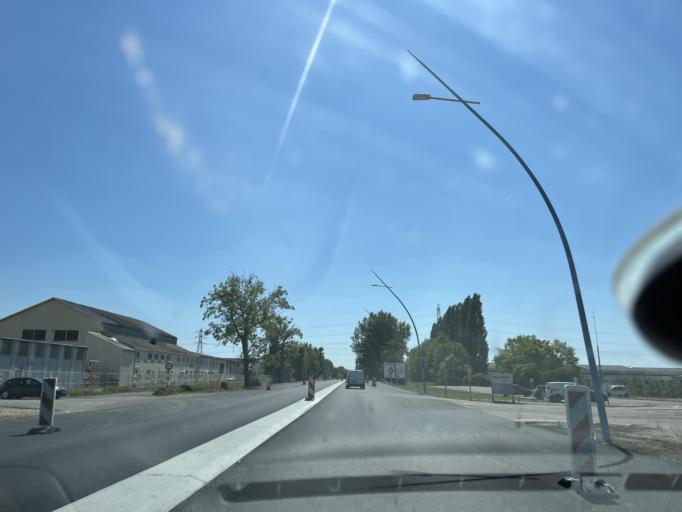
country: FR
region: Haute-Normandie
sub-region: Departement de la Seine-Maritime
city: Lillebonne
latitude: 49.4961
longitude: 0.5354
